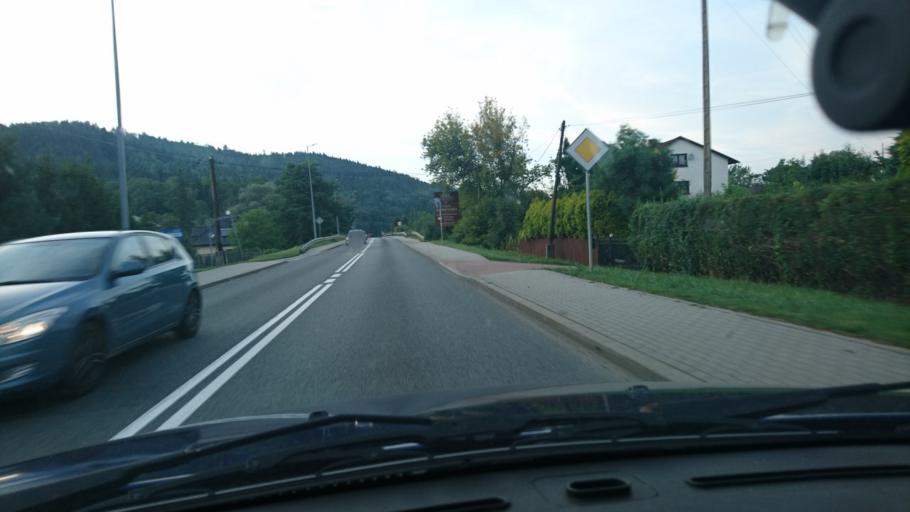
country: PL
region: Silesian Voivodeship
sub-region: Powiat zywiecki
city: Wegierska Gorka
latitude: 49.6075
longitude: 19.1164
